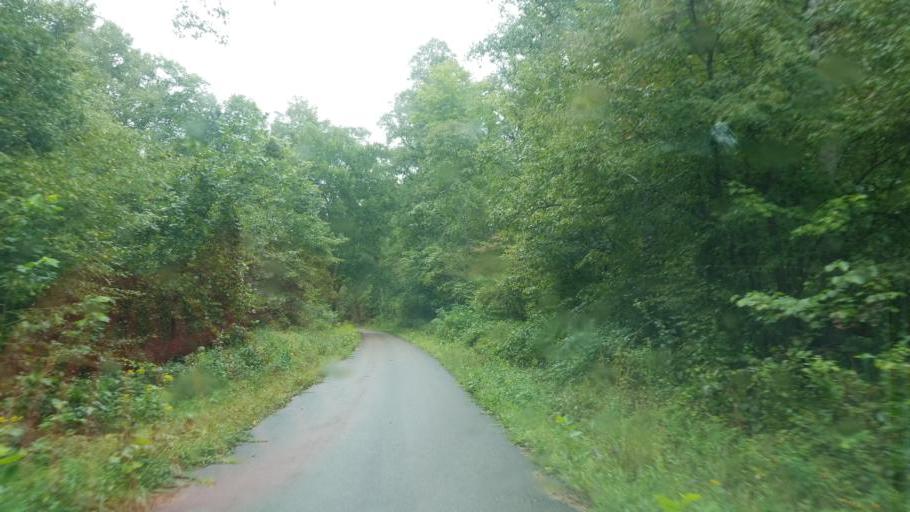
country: US
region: Ohio
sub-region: Scioto County
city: West Portsmouth
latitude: 38.7753
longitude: -83.1406
